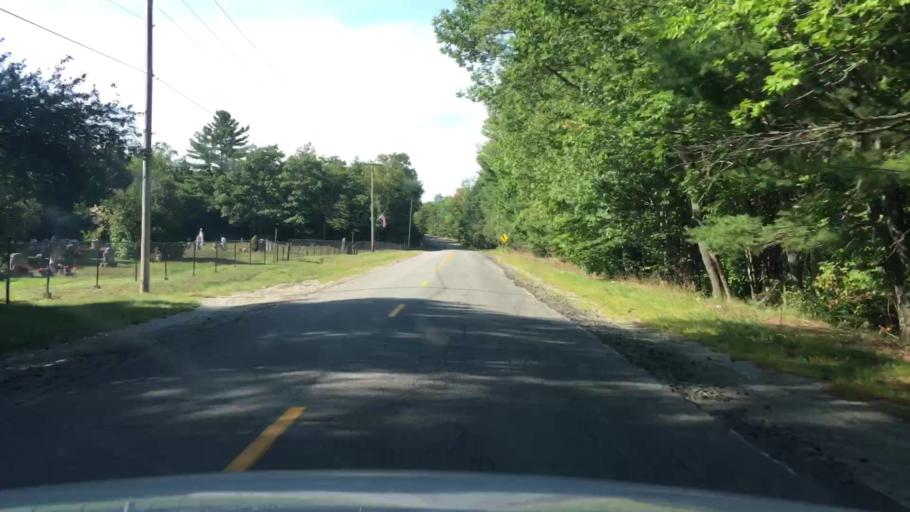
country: US
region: Maine
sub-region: Penobscot County
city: Enfield
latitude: 45.2219
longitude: -68.5373
